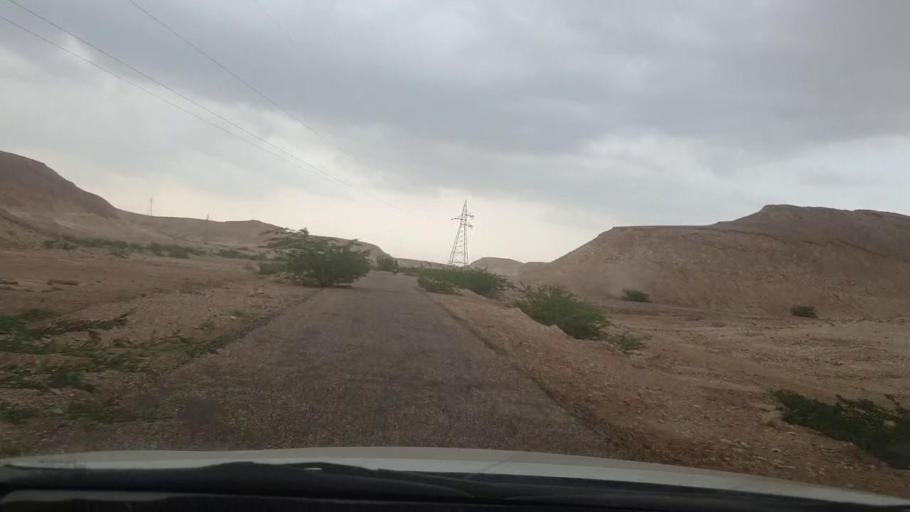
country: PK
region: Sindh
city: Khairpur
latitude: 27.4661
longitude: 68.9228
